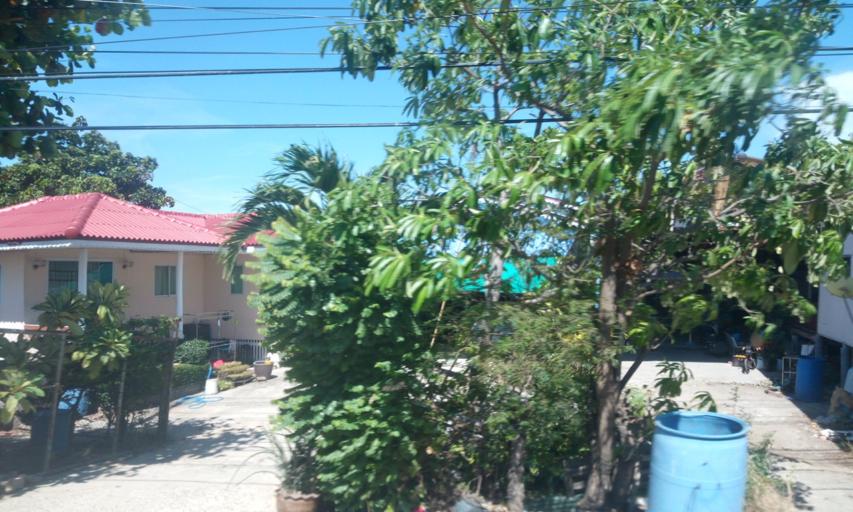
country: TH
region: Samut Prakan
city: Bang Bo District
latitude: 13.5158
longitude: 100.7885
